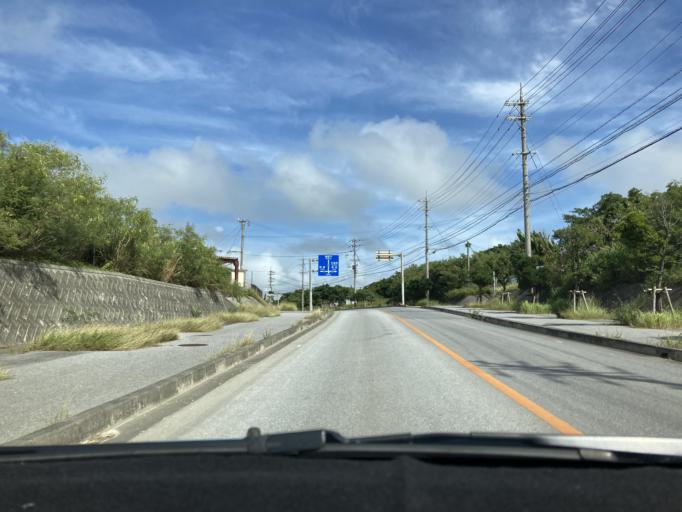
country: JP
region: Okinawa
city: Itoman
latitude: 26.1045
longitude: 127.7223
